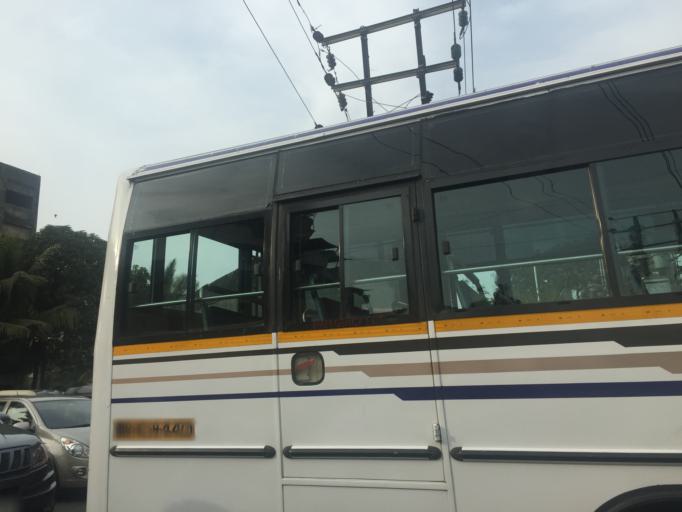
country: IN
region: Maharashtra
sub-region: Thane
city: Airoli
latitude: 19.1556
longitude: 72.9992
